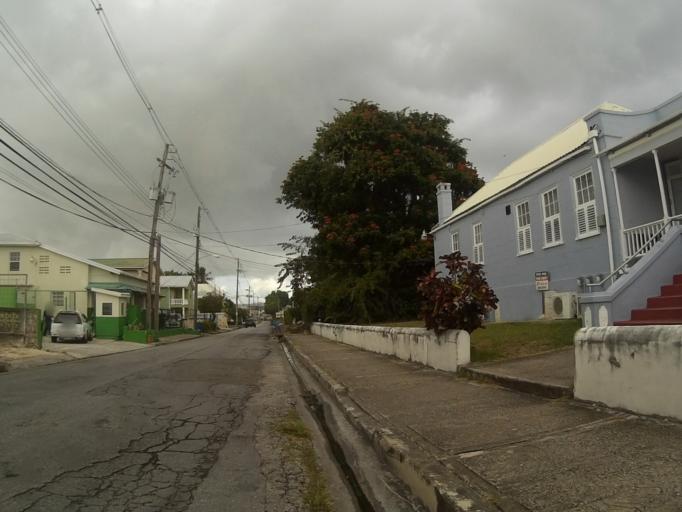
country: BB
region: Saint Michael
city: Bridgetown
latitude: 13.0971
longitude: -59.6035
